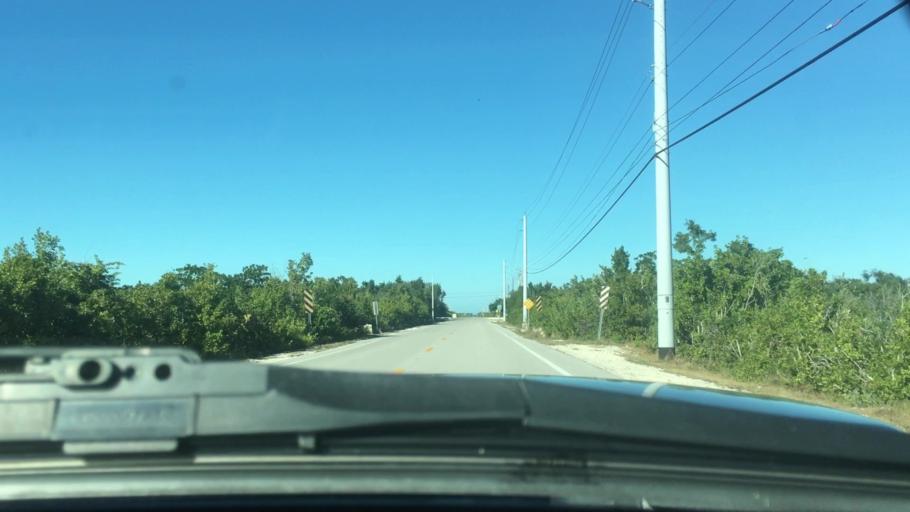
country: US
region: Florida
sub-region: Monroe County
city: Cudjoe Key
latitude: 24.6756
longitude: -81.4996
